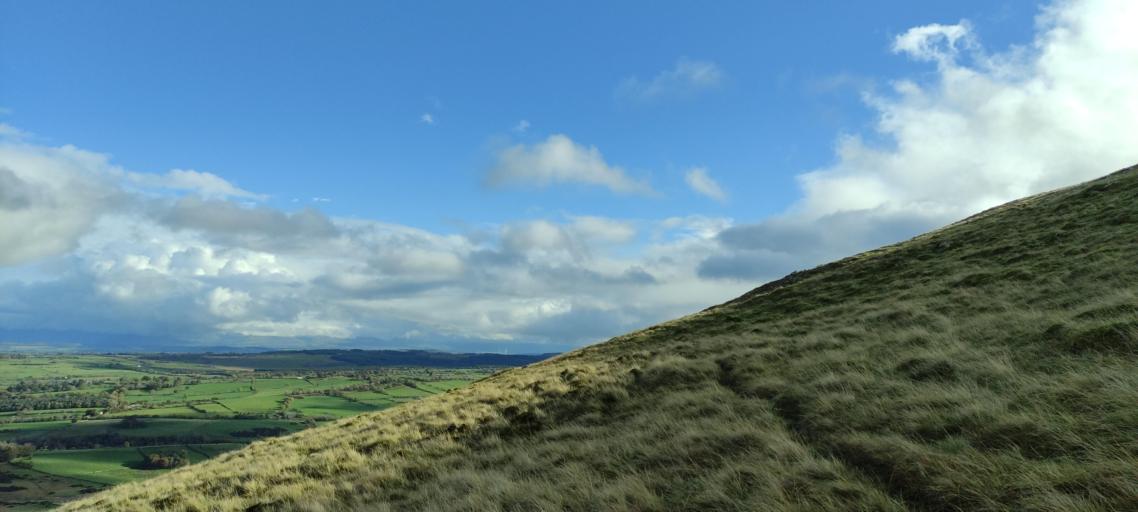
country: GB
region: England
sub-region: Cumbria
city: Keswick
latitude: 54.7001
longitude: -3.0225
